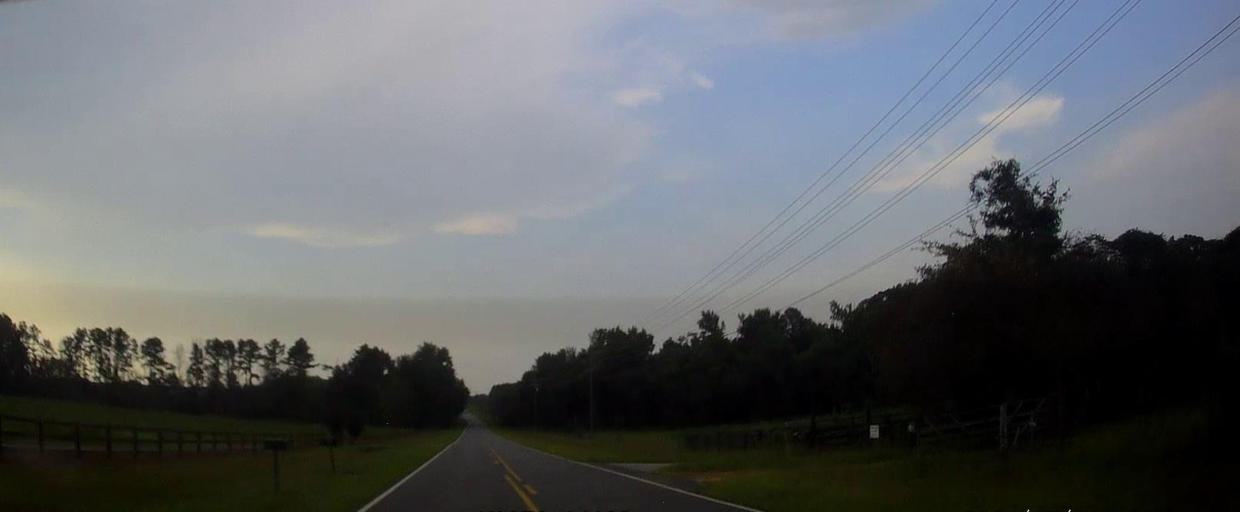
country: US
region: Georgia
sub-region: Laurens County
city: East Dublin
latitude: 32.5400
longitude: -82.8361
